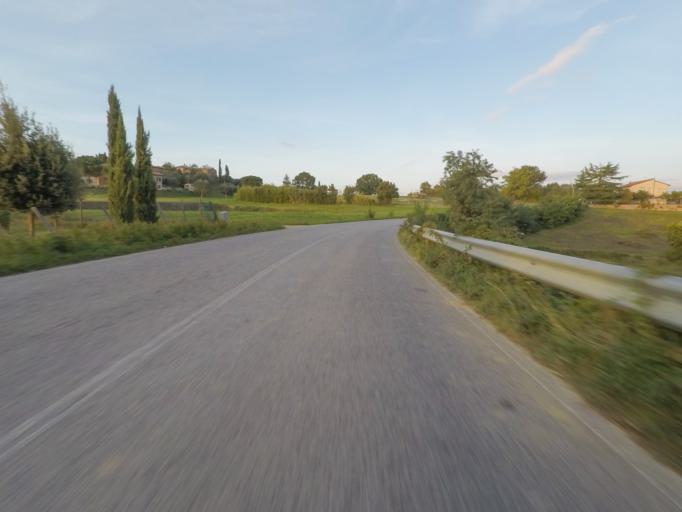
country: IT
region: Tuscany
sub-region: Provincia di Siena
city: Montepulciano
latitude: 43.1278
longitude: 11.7262
